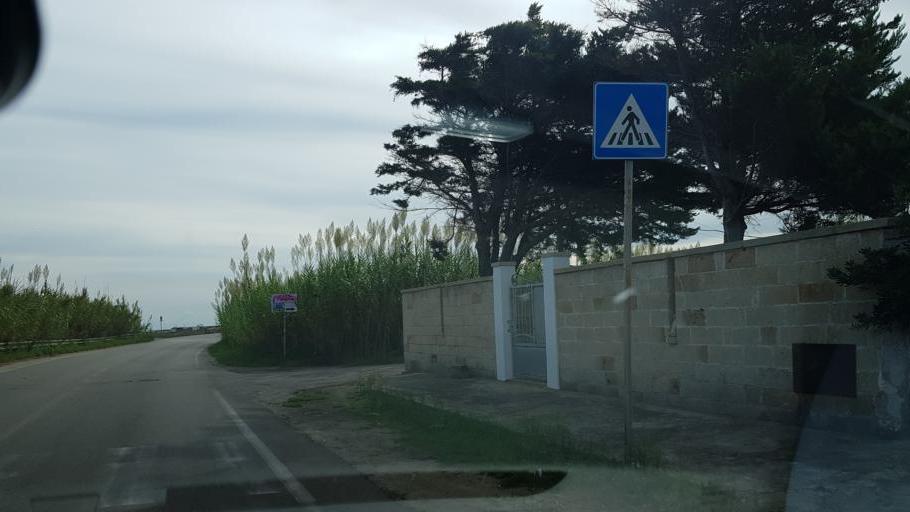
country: IT
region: Apulia
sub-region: Provincia di Lecce
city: Borgagne
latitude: 40.2965
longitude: 18.4132
